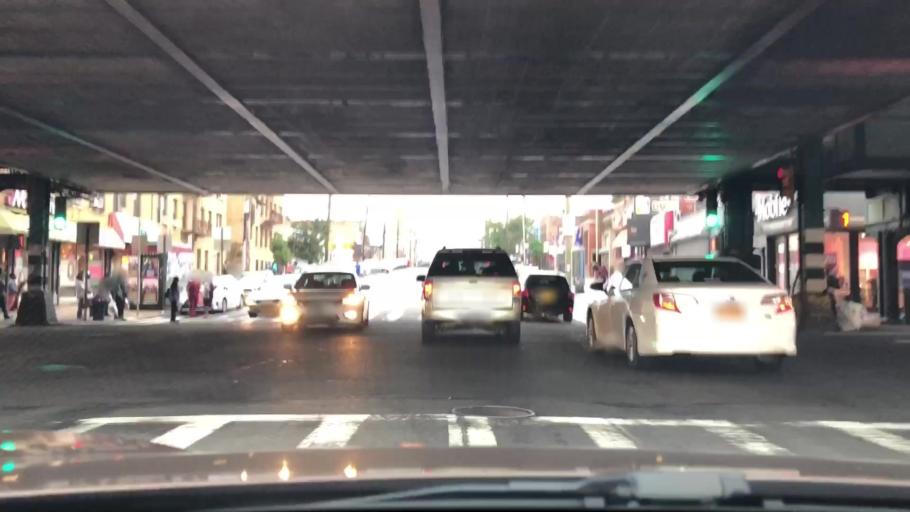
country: US
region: New York
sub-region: Bronx
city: Eastchester
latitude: 40.8934
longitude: -73.8576
